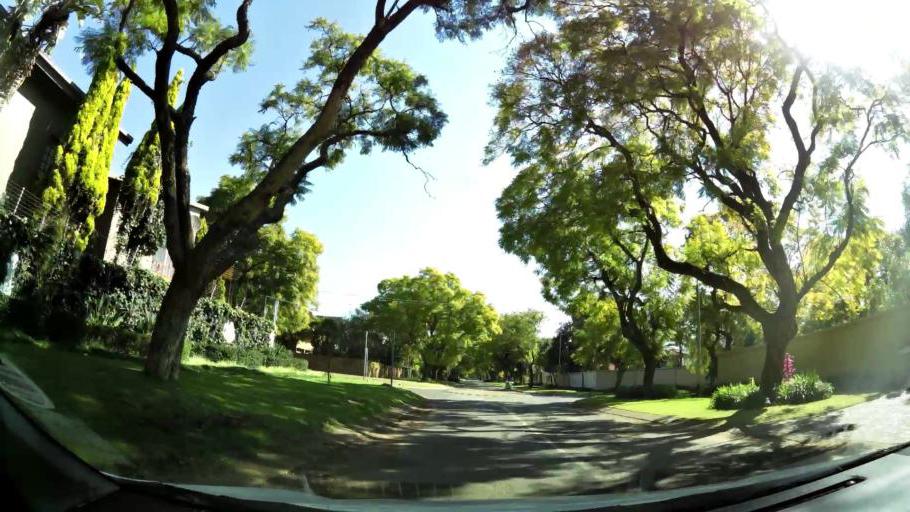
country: ZA
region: Gauteng
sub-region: City of Tshwane Metropolitan Municipality
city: Pretoria
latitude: -25.7679
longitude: 28.2462
